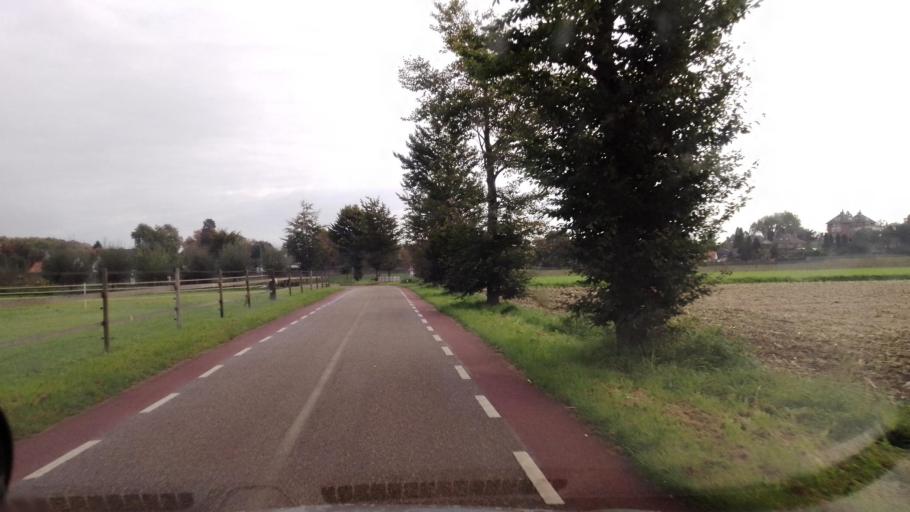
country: NL
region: Limburg
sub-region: Gemeente Venlo
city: Tegelen
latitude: 51.3318
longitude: 6.1146
